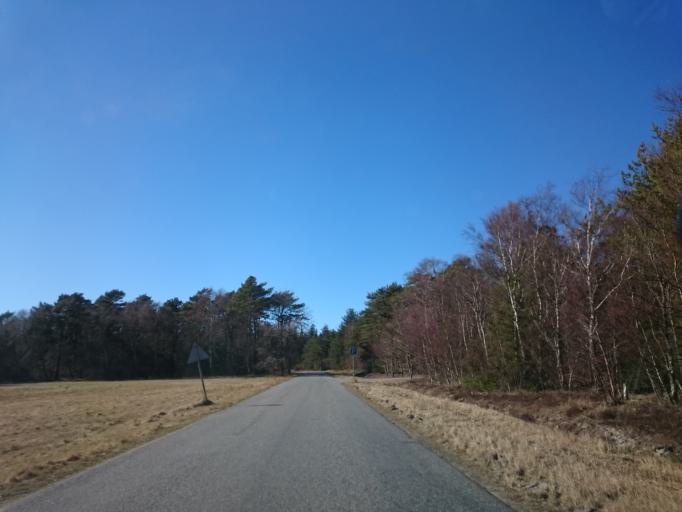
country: DK
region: North Denmark
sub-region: Frederikshavn Kommune
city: Strandby
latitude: 57.6297
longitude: 10.4366
